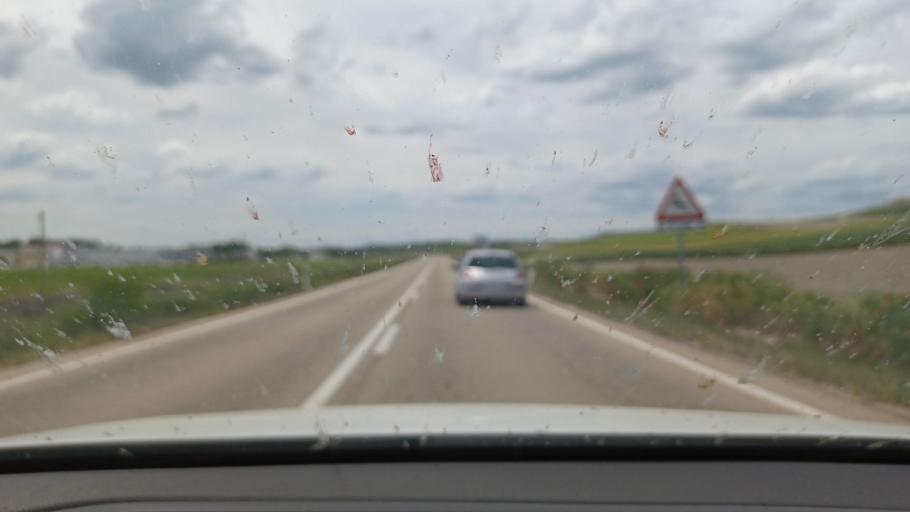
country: ES
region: Castille and Leon
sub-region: Provincia de Segovia
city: Cuellar
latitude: 41.3854
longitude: -4.2619
